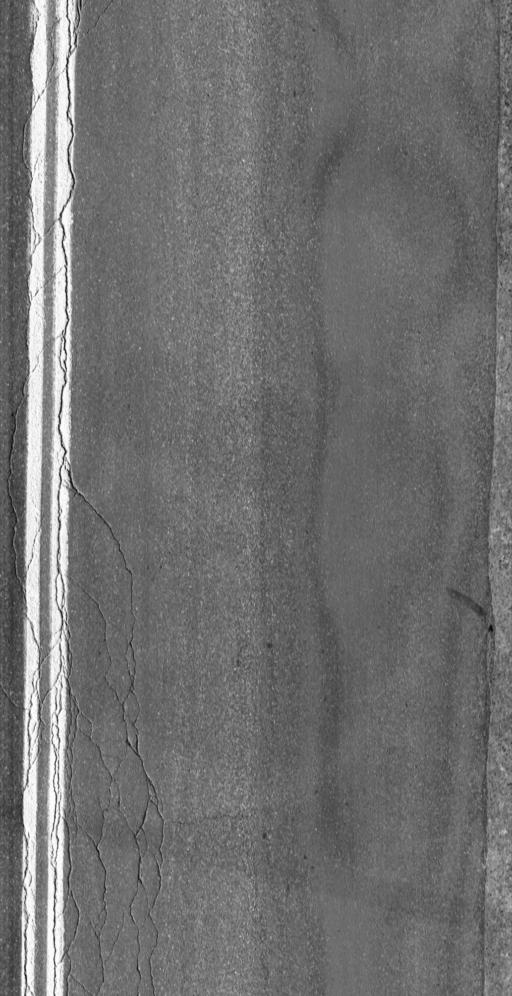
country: US
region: Vermont
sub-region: Washington County
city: South Barre
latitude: 44.1382
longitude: -72.4923
